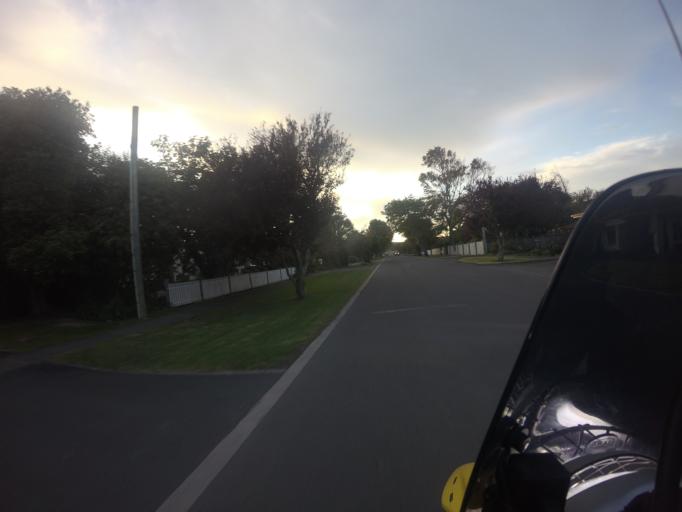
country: NZ
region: Gisborne
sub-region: Gisborne District
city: Gisborne
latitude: -38.6690
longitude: 178.0408
